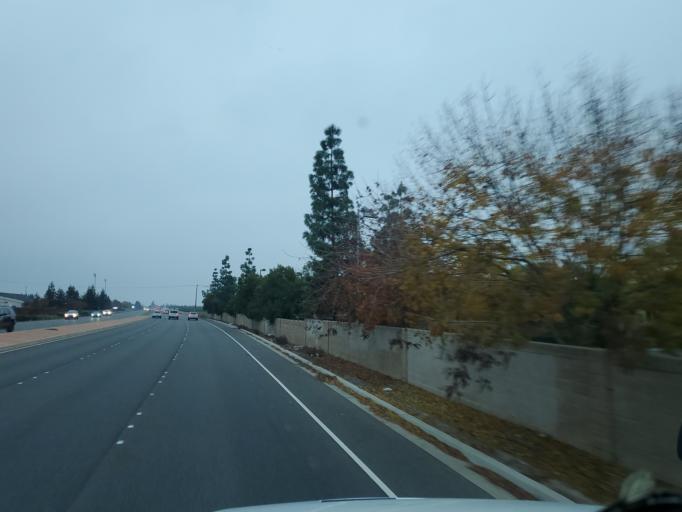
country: US
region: California
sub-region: Stanislaus County
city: Del Rio
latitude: 37.7005
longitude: -121.0012
